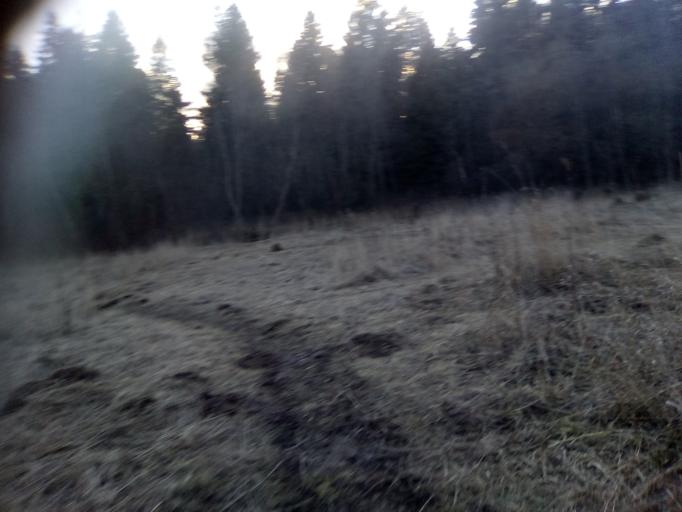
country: RU
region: Moskovskaya
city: Moskovskiy
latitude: 55.5847
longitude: 37.3391
